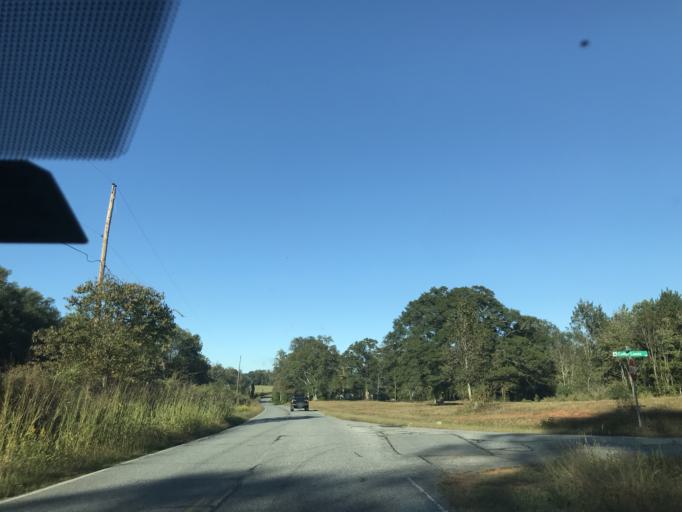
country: US
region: South Carolina
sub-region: Spartanburg County
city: Mayo
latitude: 35.1005
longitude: -81.8488
